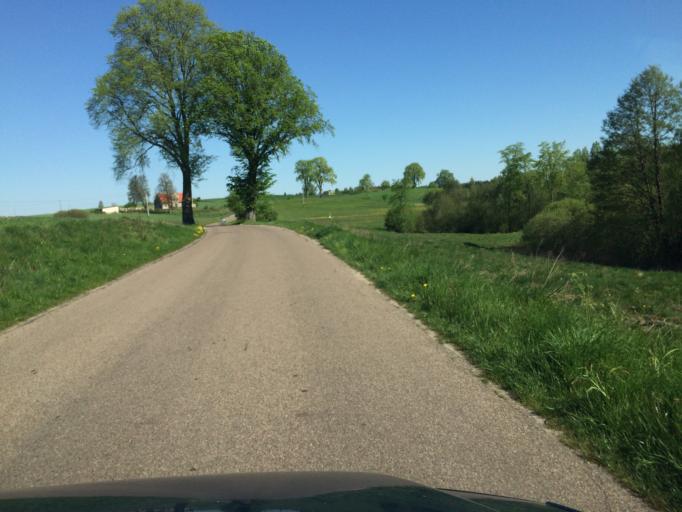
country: PL
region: Warmian-Masurian Voivodeship
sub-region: Powiat dzialdowski
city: Rybno
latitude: 53.4266
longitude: 19.9202
